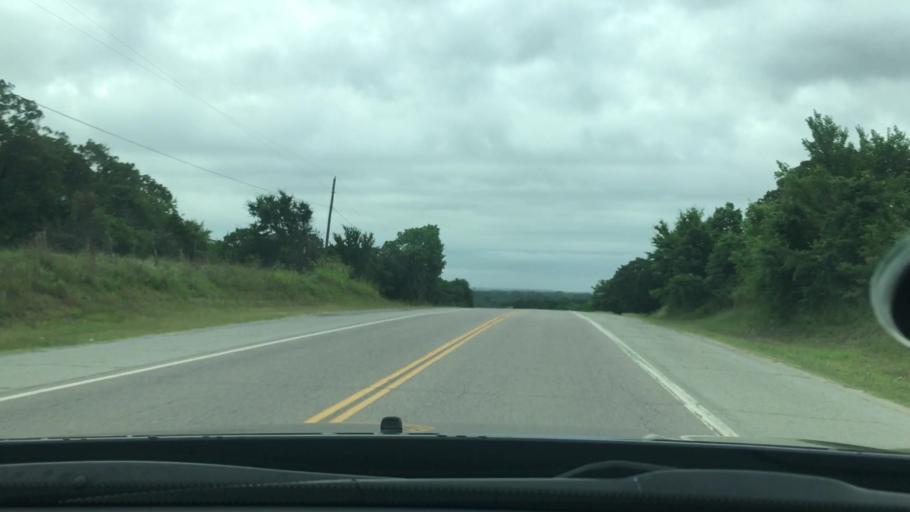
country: US
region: Oklahoma
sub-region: Coal County
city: Coalgate
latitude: 34.5559
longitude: -96.2406
